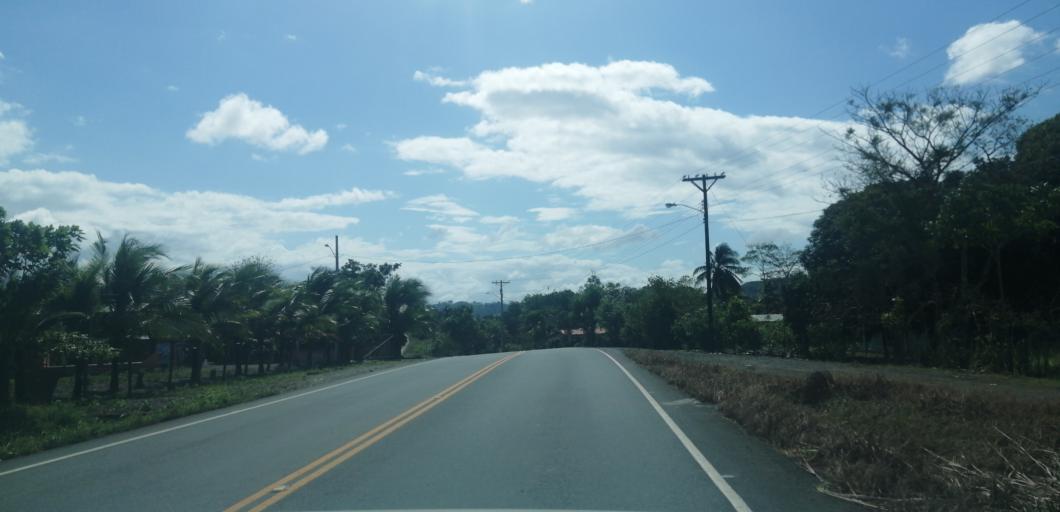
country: PA
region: Panama
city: Canita
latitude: 9.2200
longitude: -78.9172
